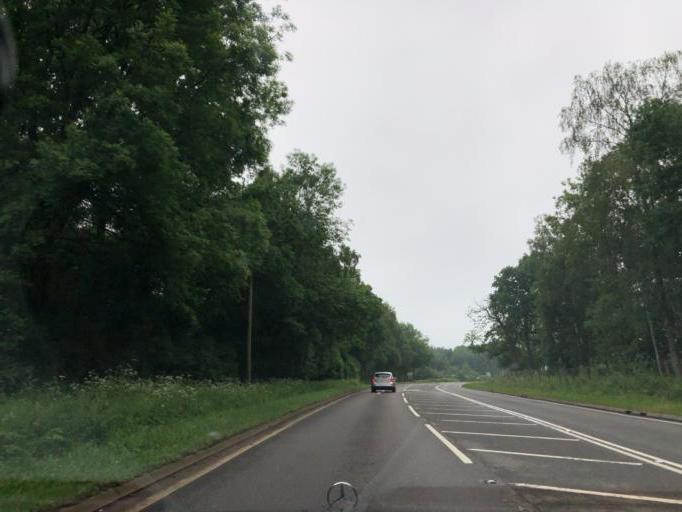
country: GB
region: England
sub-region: Warwickshire
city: Wellesbourne Mountford
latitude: 52.2303
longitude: -1.5452
